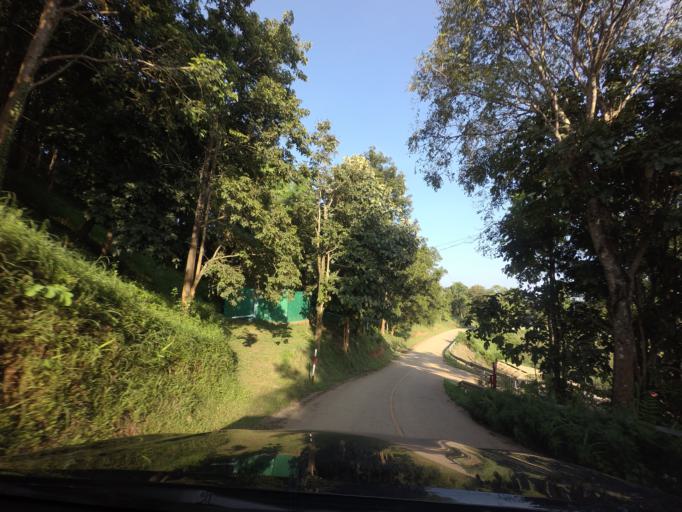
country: TH
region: Nan
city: Na Noi
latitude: 18.3752
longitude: 100.8273
